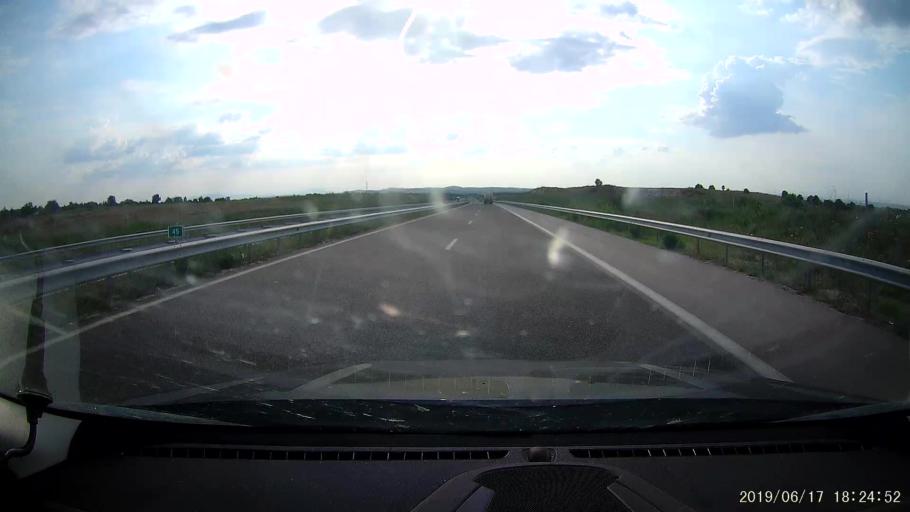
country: BG
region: Khaskovo
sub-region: Obshtina Dimitrovgrad
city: Dimitrovgrad
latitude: 41.9880
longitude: 25.6789
